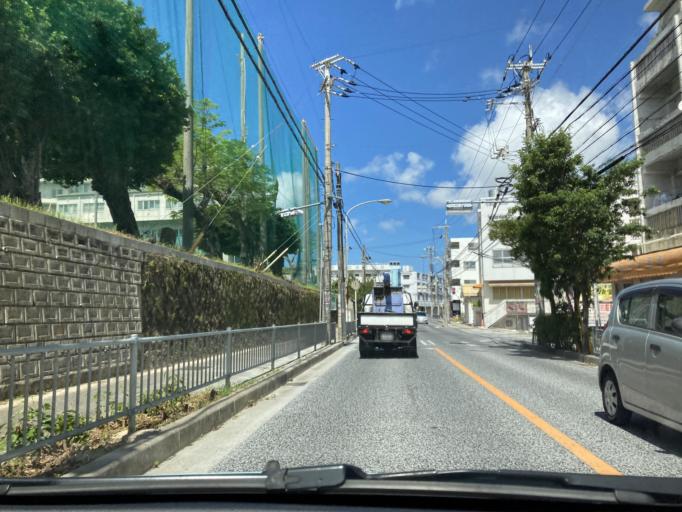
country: JP
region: Okinawa
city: Naha-shi
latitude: 26.2001
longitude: 127.7005
